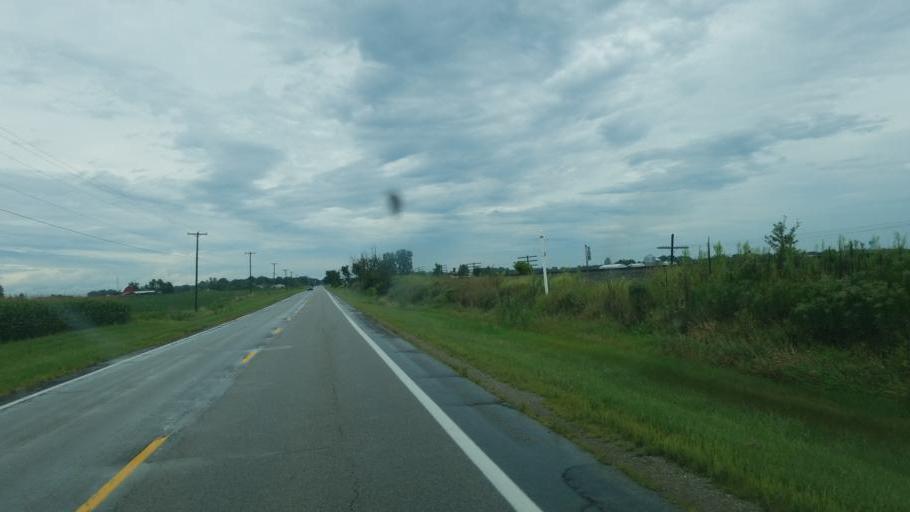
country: US
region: Ohio
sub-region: Delaware County
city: Ashley
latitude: 40.3886
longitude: -82.9688
